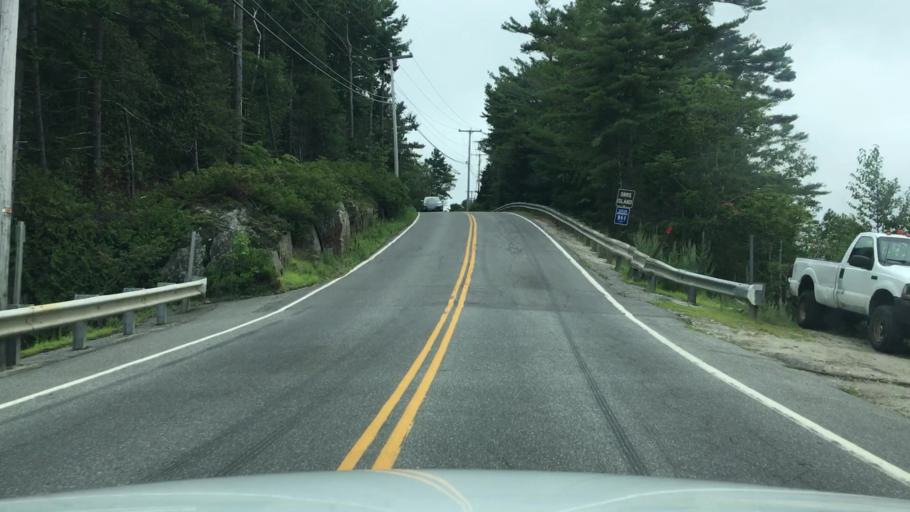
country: US
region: Maine
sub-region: Cumberland County
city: Harpswell Center
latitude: 43.7947
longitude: -69.9462
